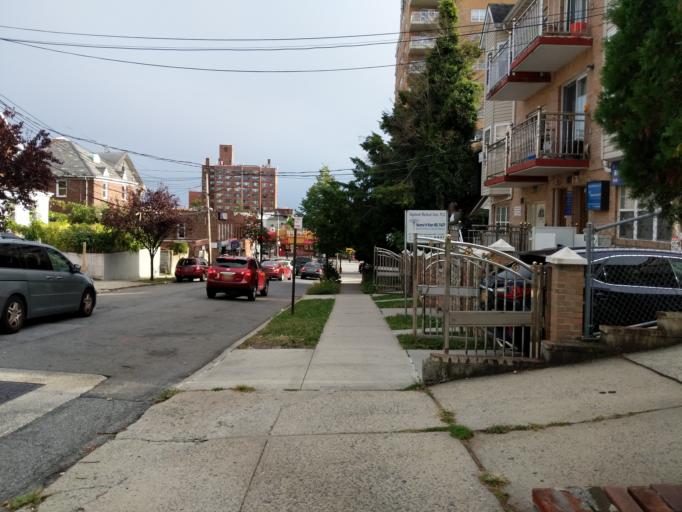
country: US
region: New York
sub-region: Queens County
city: Jamaica
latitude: 40.7107
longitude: -73.7962
